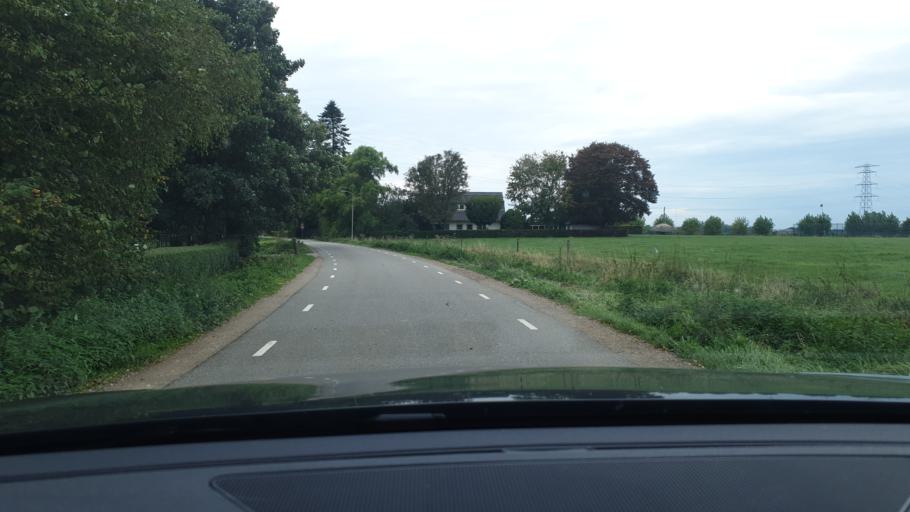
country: NL
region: Gelderland
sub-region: Gemeente Overbetuwe
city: Oosterhout
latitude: 51.8985
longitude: 5.8332
